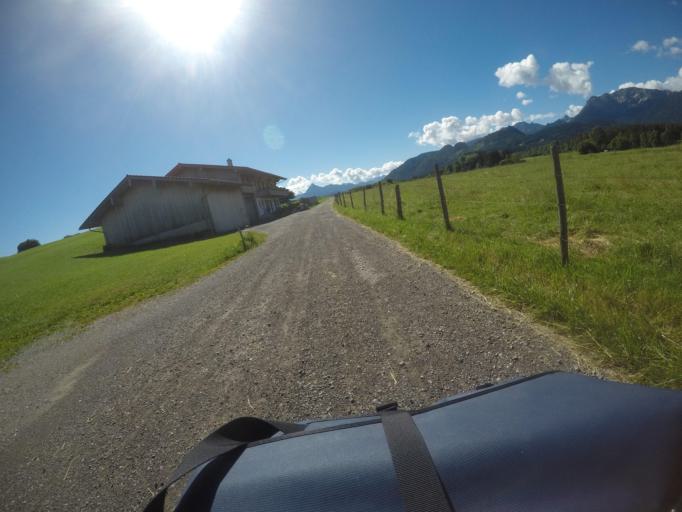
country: DE
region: Bavaria
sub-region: Swabia
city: Pfronten
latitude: 47.5956
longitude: 10.5724
